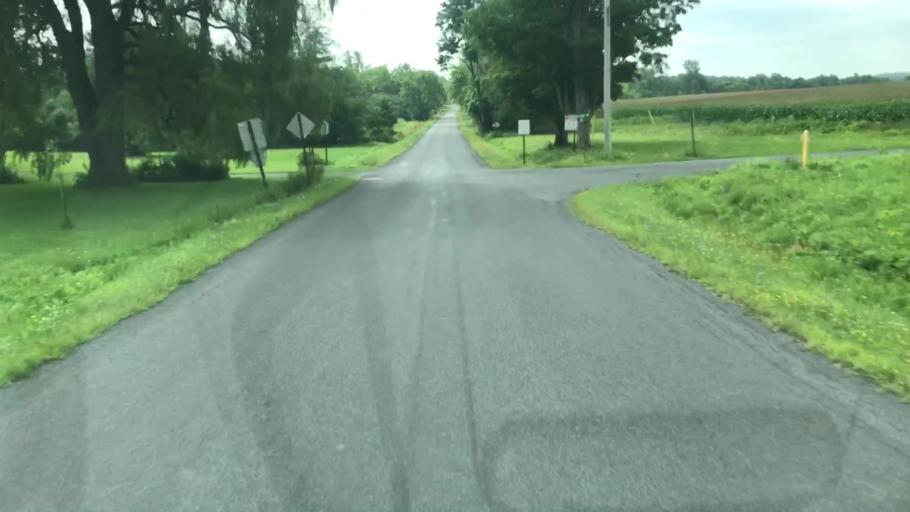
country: US
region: New York
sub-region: Cayuga County
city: Melrose Park
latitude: 42.9280
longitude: -76.5084
